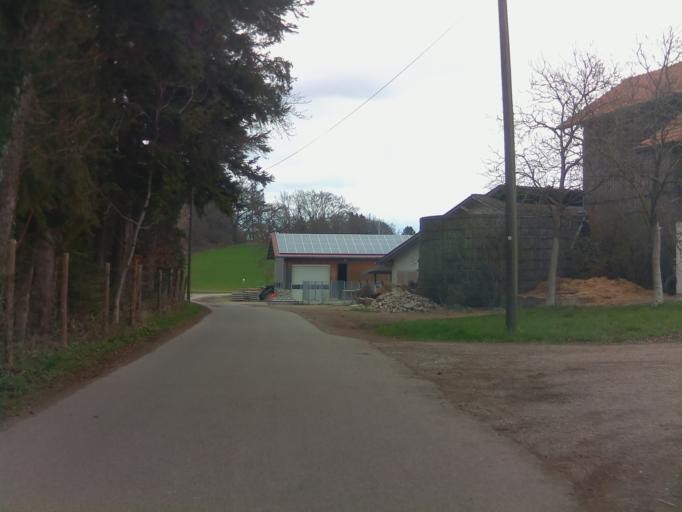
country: DE
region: Bavaria
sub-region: Upper Bavaria
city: Pahl
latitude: 47.9372
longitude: 11.2079
